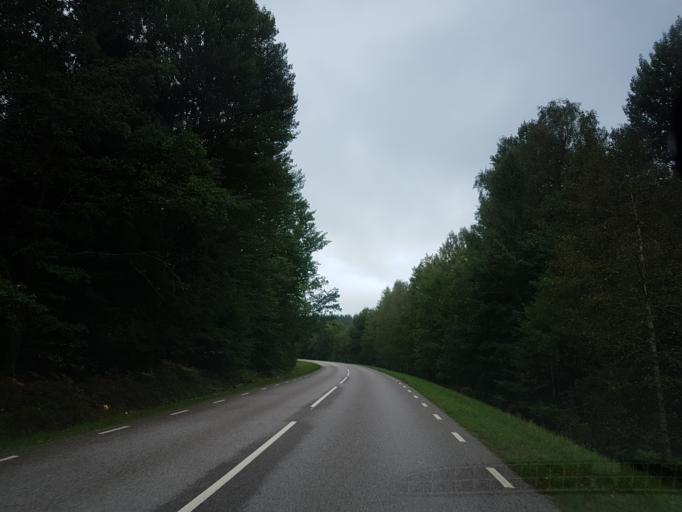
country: SE
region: OEstergoetland
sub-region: Atvidabergs Kommun
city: Atvidaberg
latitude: 58.2308
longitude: 16.0020
